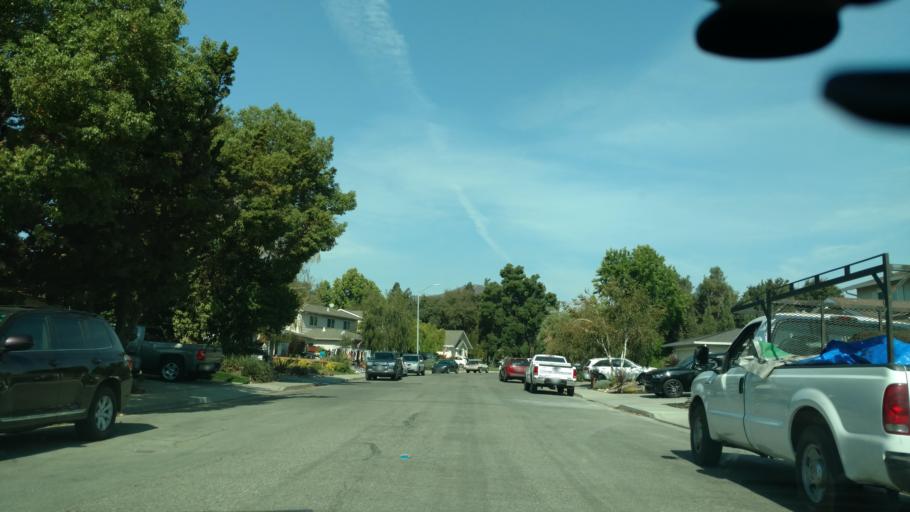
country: US
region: California
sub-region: Santa Clara County
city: Morgan Hill
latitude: 37.1046
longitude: -121.6476
